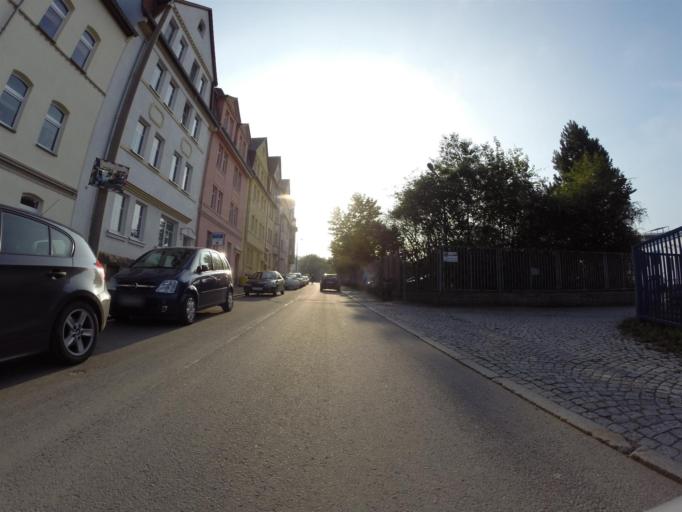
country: DE
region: Thuringia
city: Jena
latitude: 50.9157
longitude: 11.5732
